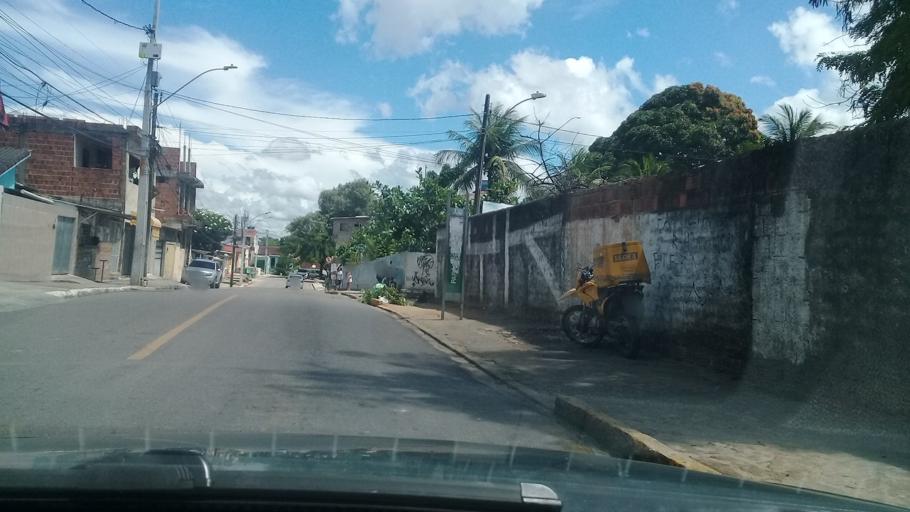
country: BR
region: Pernambuco
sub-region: Jaboatao Dos Guararapes
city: Jaboatao dos Guararapes
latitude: -8.1214
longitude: -34.9462
